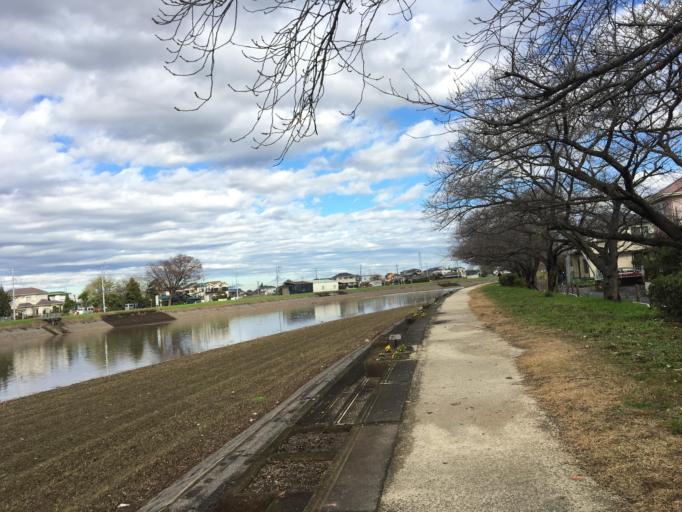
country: JP
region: Saitama
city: Koshigaya
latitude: 35.9234
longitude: 139.8057
